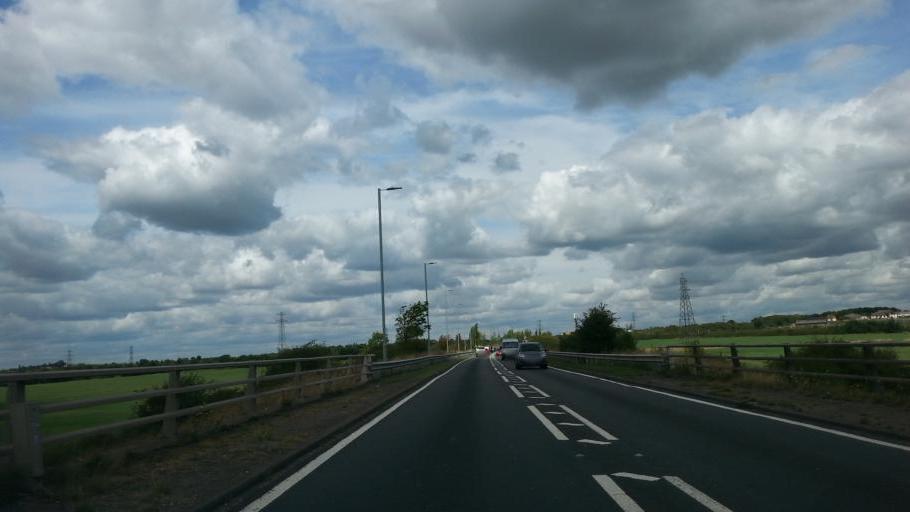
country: GB
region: England
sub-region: Essex
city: South Benfleet
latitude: 51.5486
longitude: 0.5423
